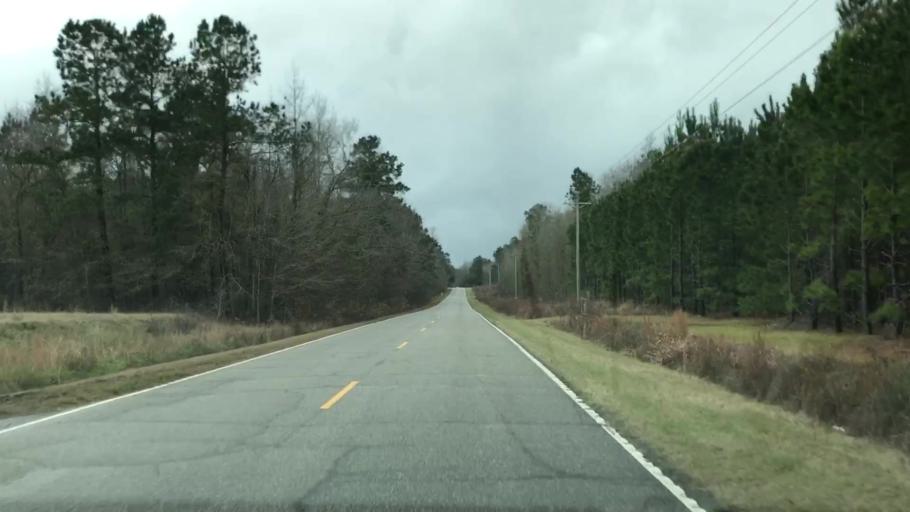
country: US
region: South Carolina
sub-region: Florence County
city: Johnsonville
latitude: 33.6647
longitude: -79.4077
